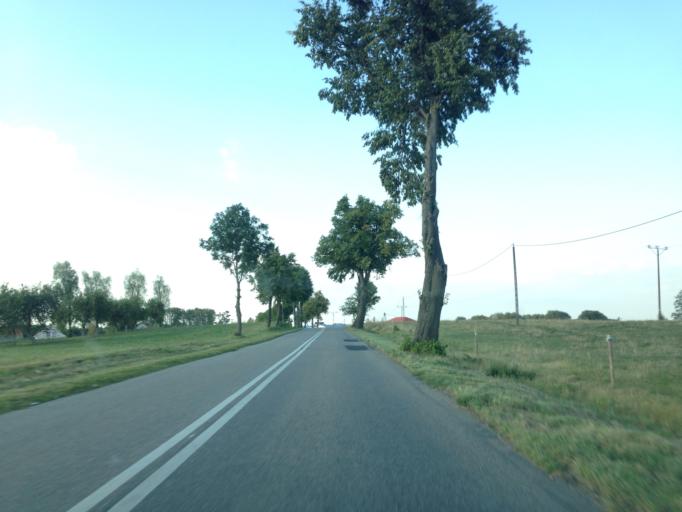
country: PL
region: Warmian-Masurian Voivodeship
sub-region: Powiat ilawski
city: Susz
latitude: 53.7315
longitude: 19.3522
